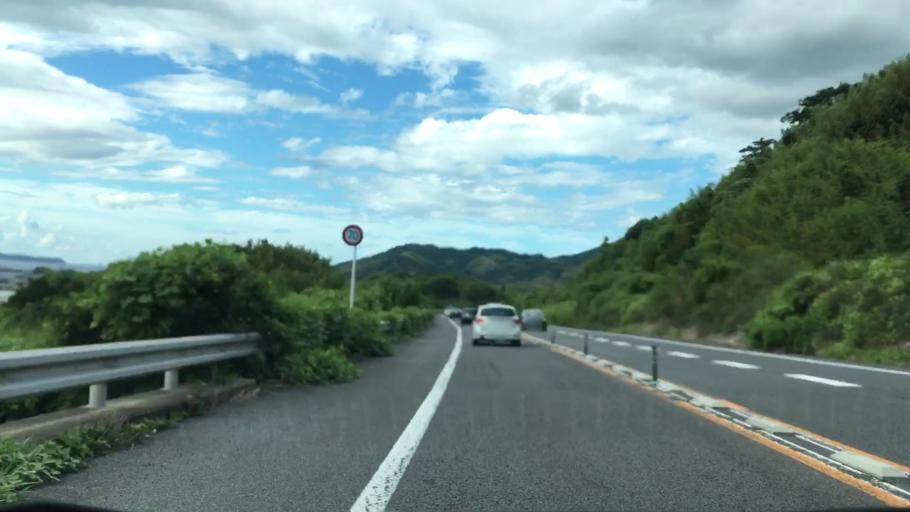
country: JP
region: Saga Prefecture
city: Karatsu
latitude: 33.4334
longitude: 130.0483
